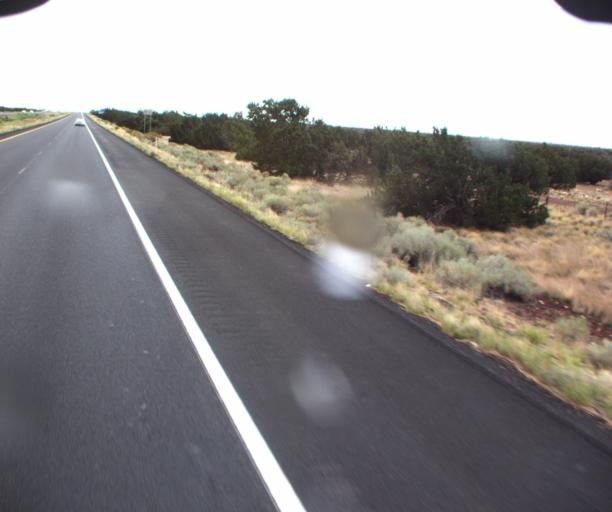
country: US
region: Arizona
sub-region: Coconino County
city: Flagstaff
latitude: 35.1638
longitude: -111.3124
